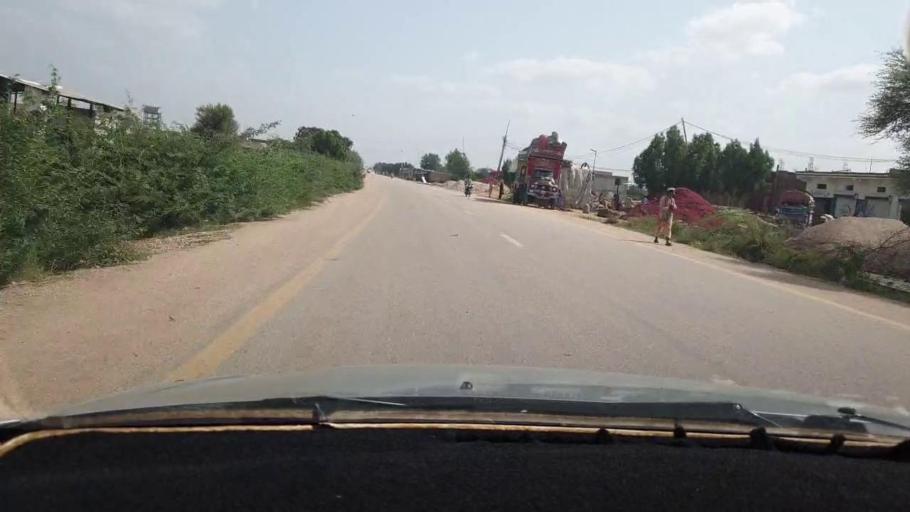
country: PK
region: Sindh
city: Naukot
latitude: 24.9770
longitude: 69.2948
